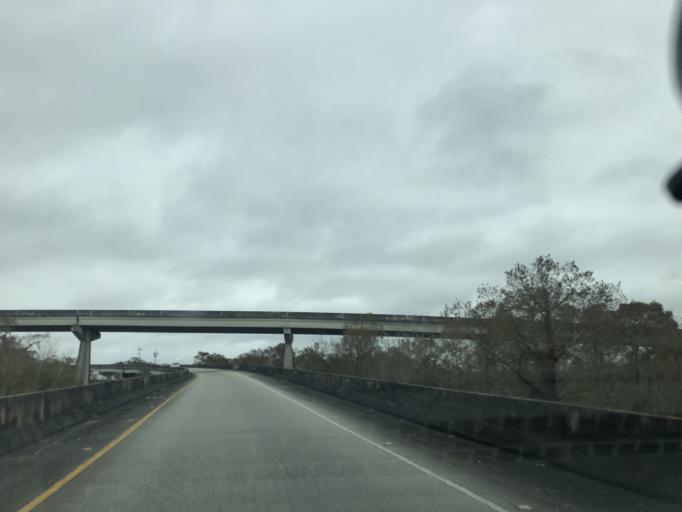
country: US
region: Louisiana
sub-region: Saint Charles Parish
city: Saint Rose
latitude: 29.9754
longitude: -90.3229
